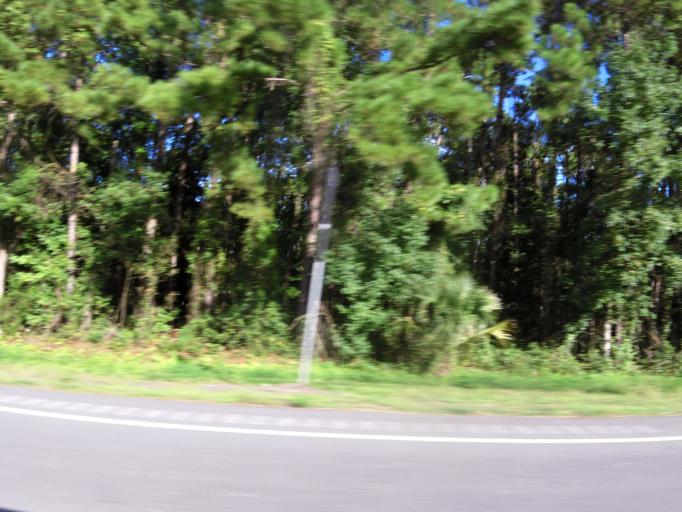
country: US
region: Georgia
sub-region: Glynn County
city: Country Club Estates
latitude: 31.2217
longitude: -81.4618
